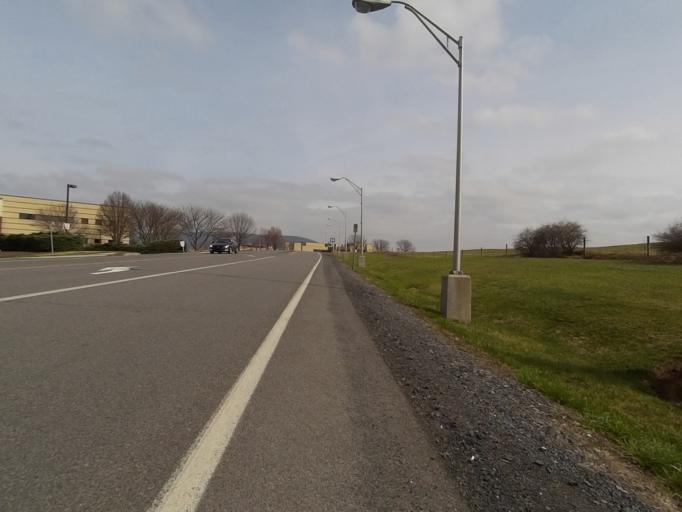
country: US
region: Pennsylvania
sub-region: Centre County
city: Houserville
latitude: 40.8201
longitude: -77.8472
